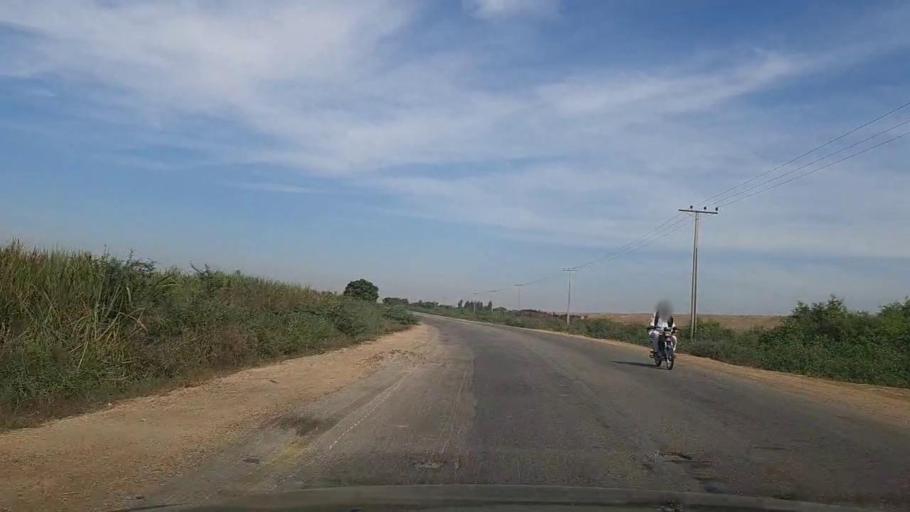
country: PK
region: Sindh
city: Daro Mehar
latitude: 24.9329
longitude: 68.1059
